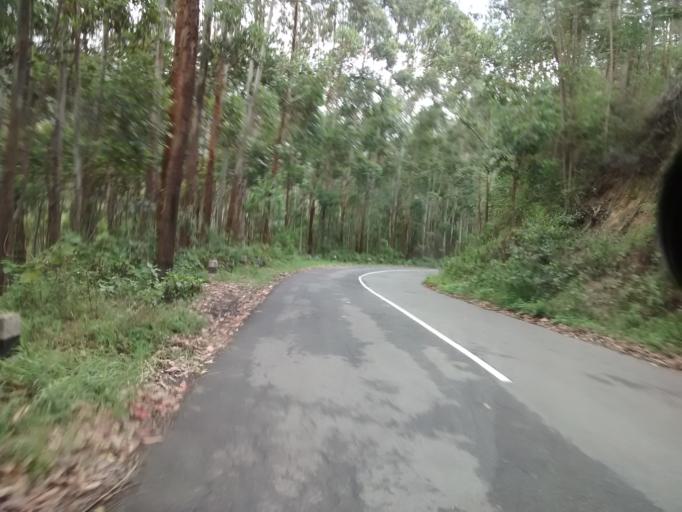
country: IN
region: Kerala
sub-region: Idukki
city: Munnar
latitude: 10.1217
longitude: 77.1463
